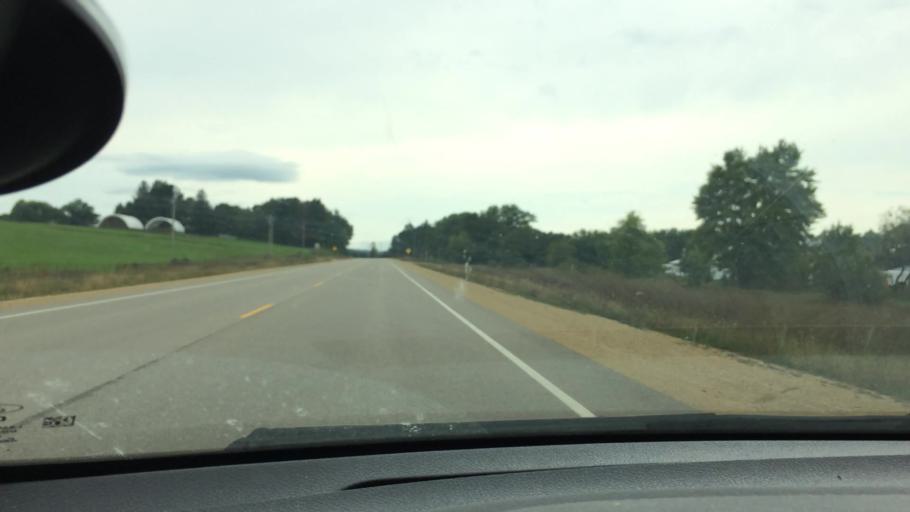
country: US
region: Wisconsin
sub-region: Trempealeau County
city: Osseo
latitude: 44.5894
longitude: -91.1671
